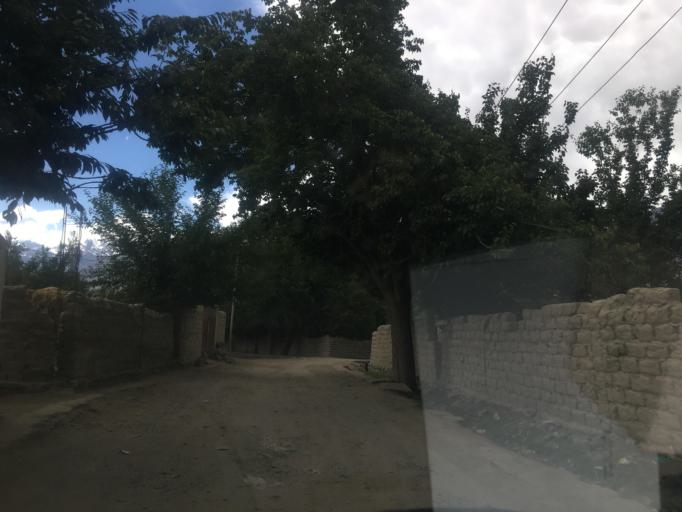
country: PK
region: Gilgit-Baltistan
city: Skardu
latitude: 35.3140
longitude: 75.5439
